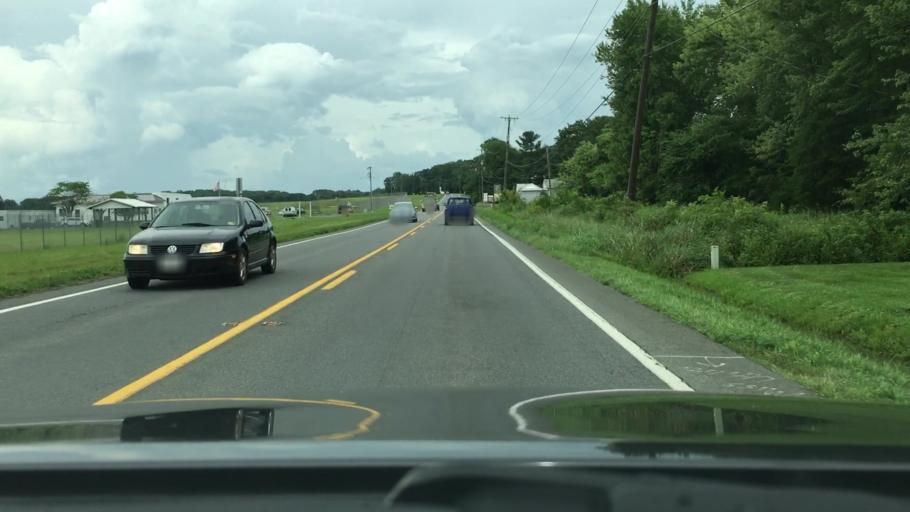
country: US
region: Virginia
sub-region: Orange County
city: Orange
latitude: 38.2457
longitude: -78.0459
